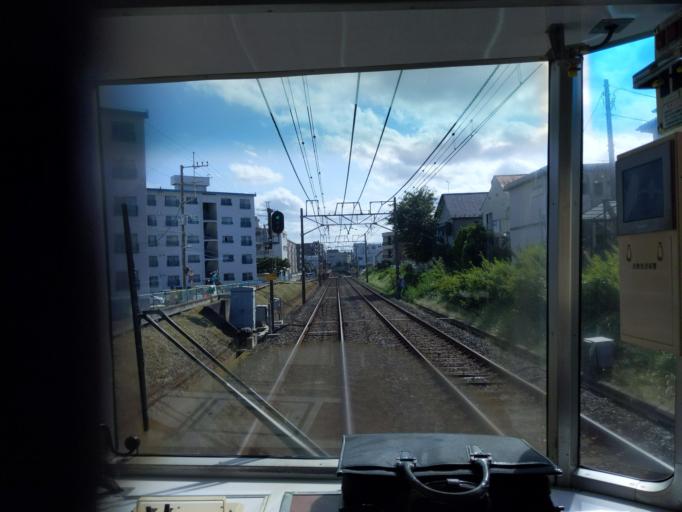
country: JP
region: Chiba
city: Funabashi
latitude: 35.7179
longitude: 140.0437
